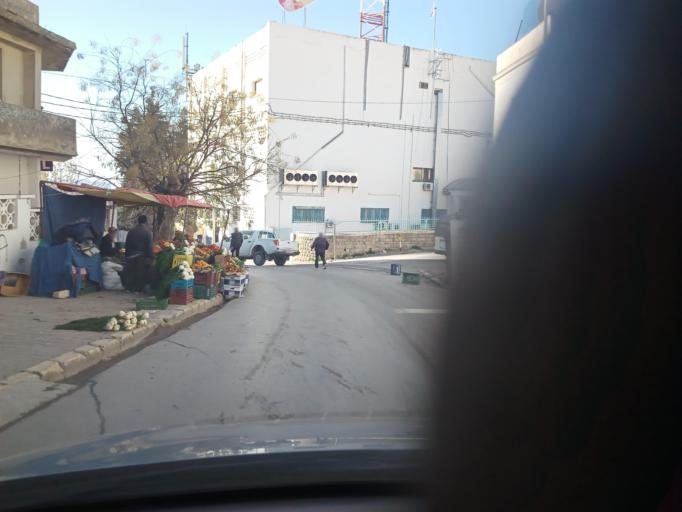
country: TN
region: Kef
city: El Kef
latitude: 36.1805
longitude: 8.7090
